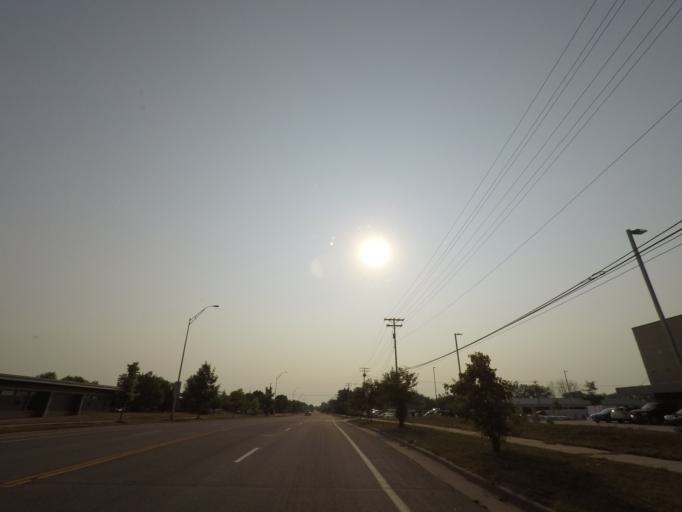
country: US
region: Wisconsin
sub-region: Dane County
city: McFarland
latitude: 43.0517
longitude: -89.2881
